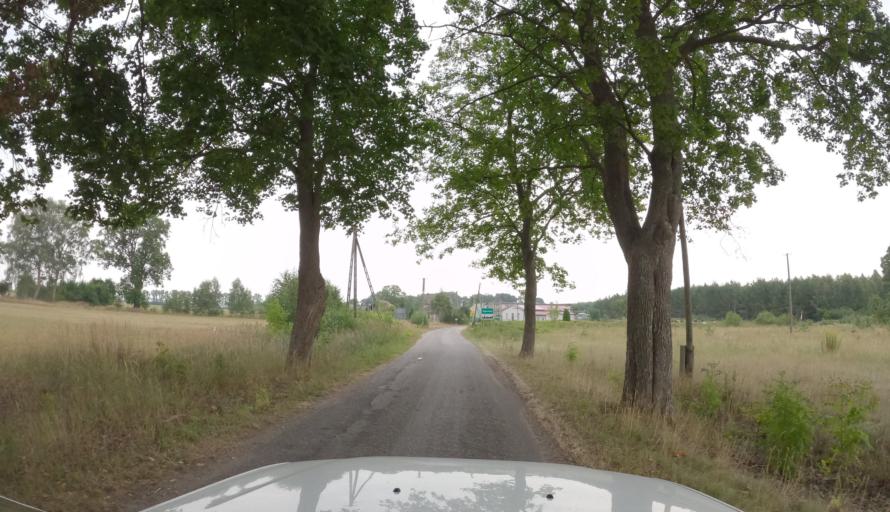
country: PL
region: West Pomeranian Voivodeship
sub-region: Powiat kolobrzeski
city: Ryman
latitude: 53.8419
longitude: 15.5917
